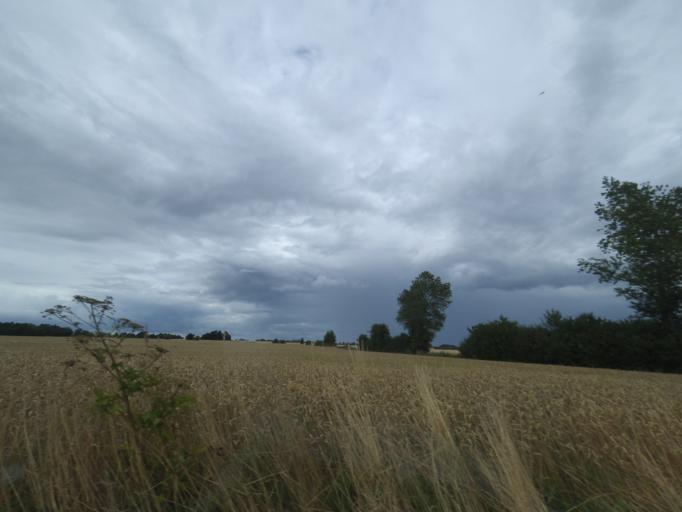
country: DK
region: South Denmark
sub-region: Nordfyns Kommune
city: Otterup
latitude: 55.4850
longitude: 10.3697
